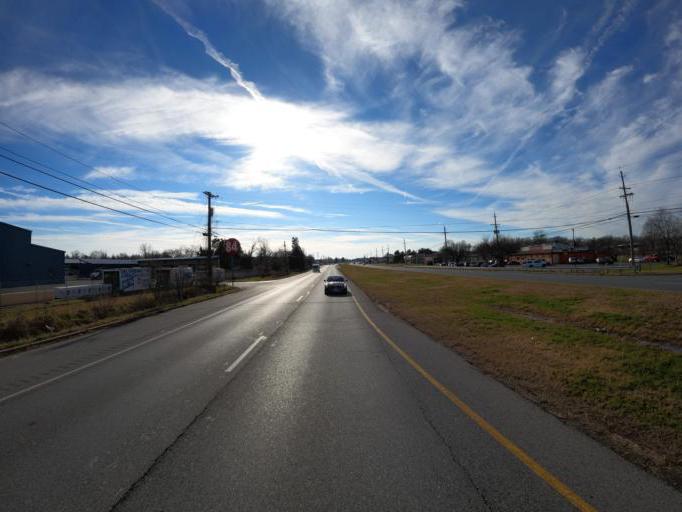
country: US
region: Maryland
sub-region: Charles County
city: Saint Charles
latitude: 38.5902
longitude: -76.9422
